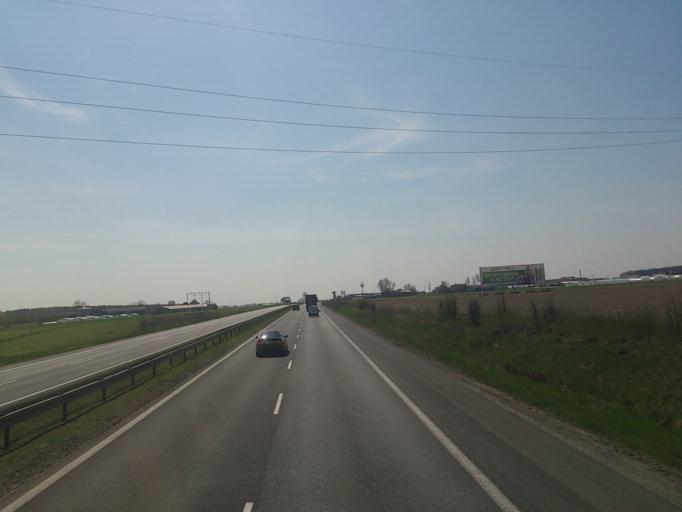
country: PL
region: Lodz Voivodeship
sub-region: Powiat piotrkowski
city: Wola Krzysztoporska
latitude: 51.3959
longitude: 19.6302
